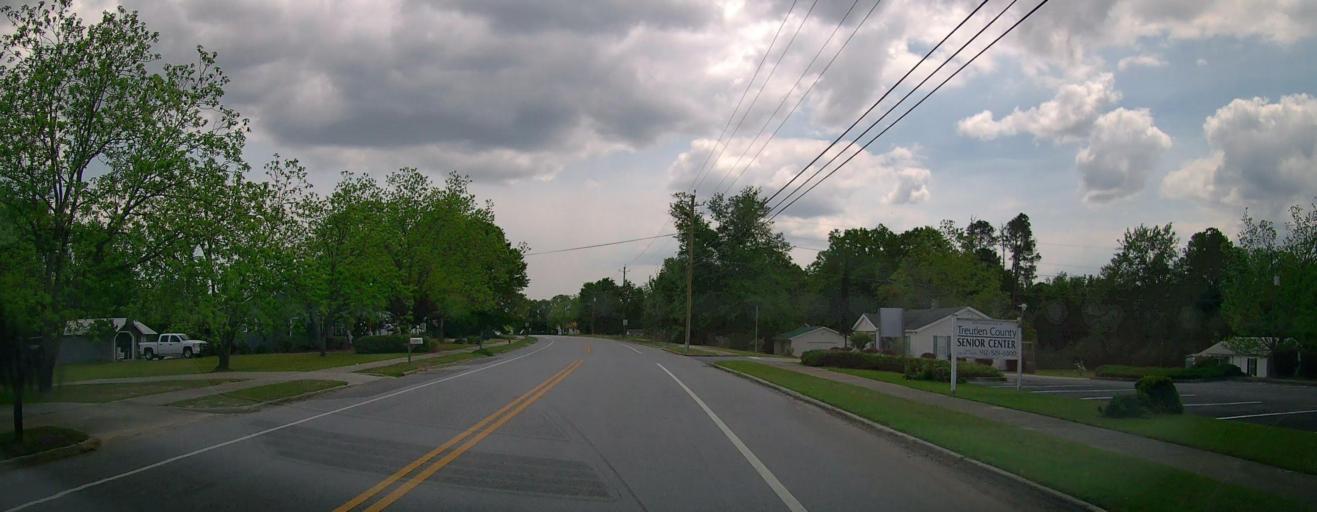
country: US
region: Georgia
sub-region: Treutlen County
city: Soperton
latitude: 32.3831
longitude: -82.5959
